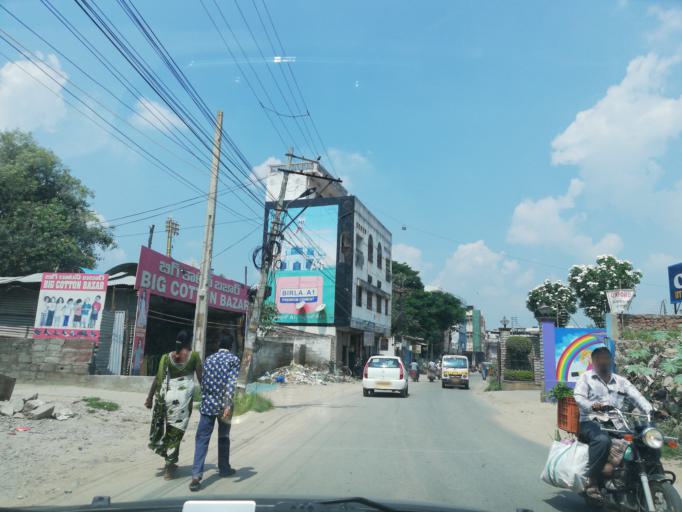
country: IN
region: Telangana
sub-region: Medak
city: Serilingampalle
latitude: 17.4905
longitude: 78.3178
